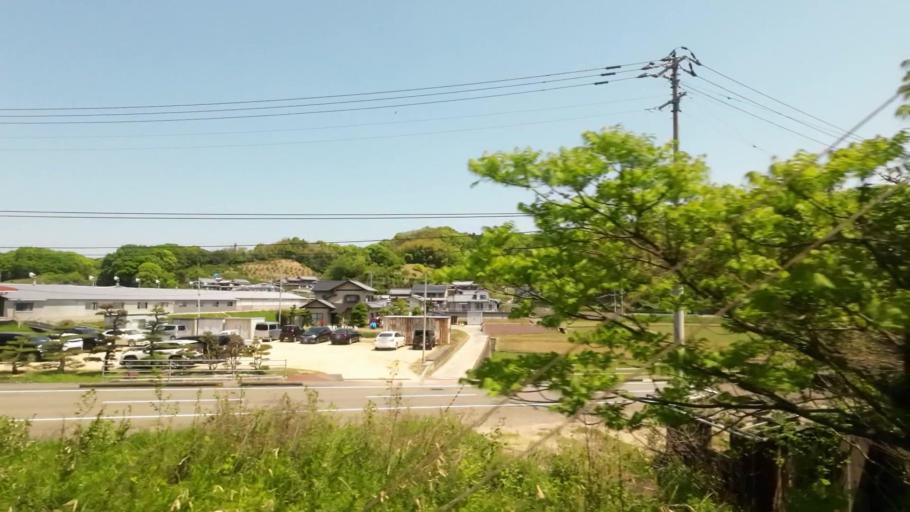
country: JP
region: Ehime
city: Hojo
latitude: 34.0956
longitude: 132.9397
